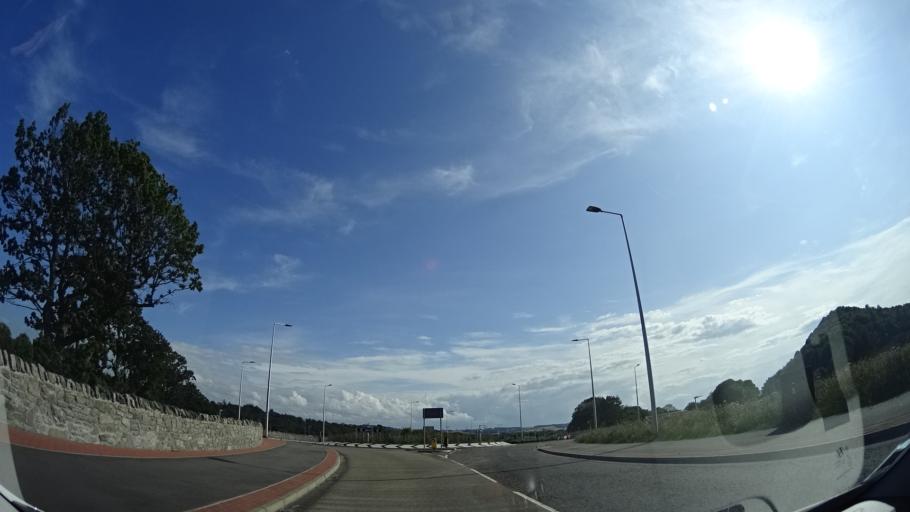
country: GB
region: Scotland
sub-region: Highland
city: Inverness
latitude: 57.4638
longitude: -4.2426
